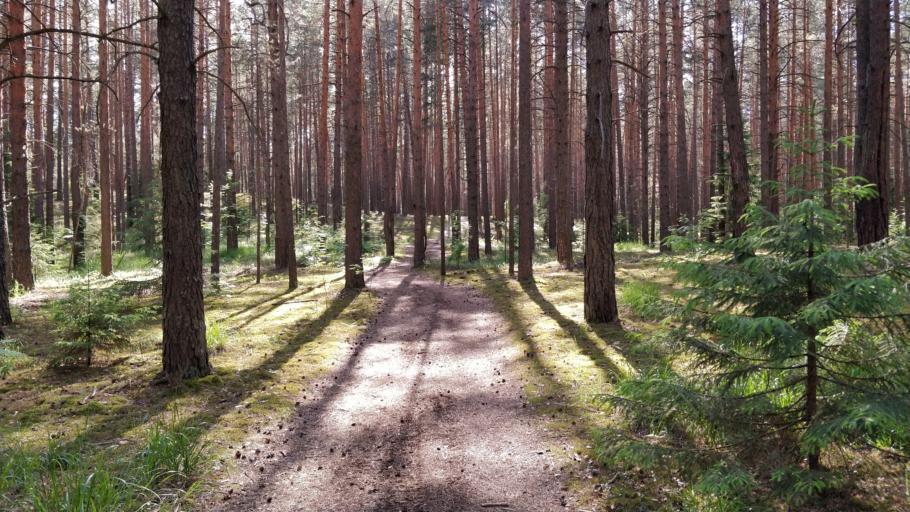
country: RU
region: Perm
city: Perm
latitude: 58.0692
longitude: 56.2896
